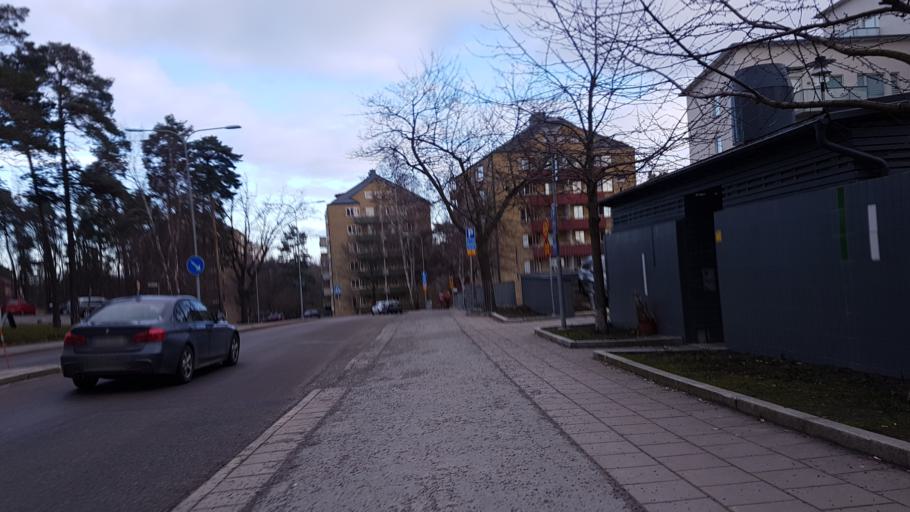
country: SE
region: Stockholm
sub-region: Lidingo
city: Lidingoe
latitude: 59.3512
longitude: 18.1385
